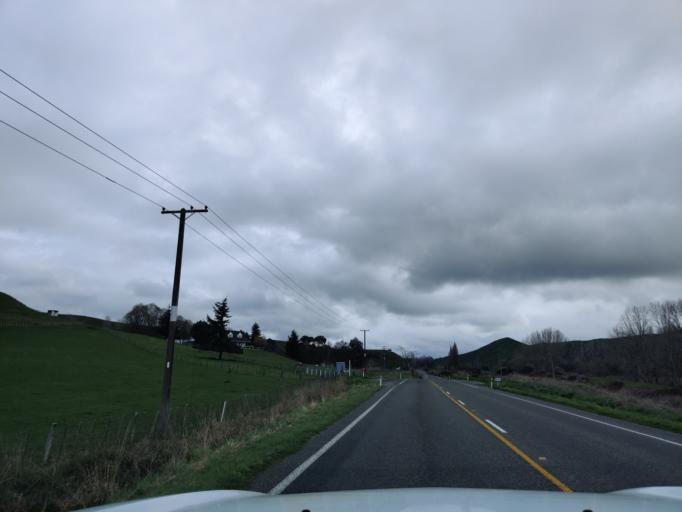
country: NZ
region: Manawatu-Wanganui
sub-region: Ruapehu District
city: Waiouru
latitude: -39.7072
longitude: 175.8335
